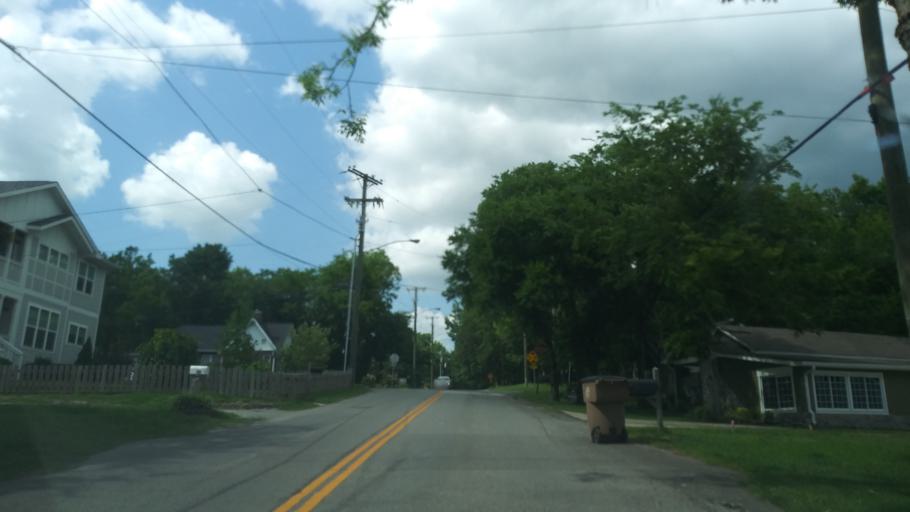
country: US
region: Tennessee
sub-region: Davidson County
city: Nashville
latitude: 36.1418
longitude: -86.8290
